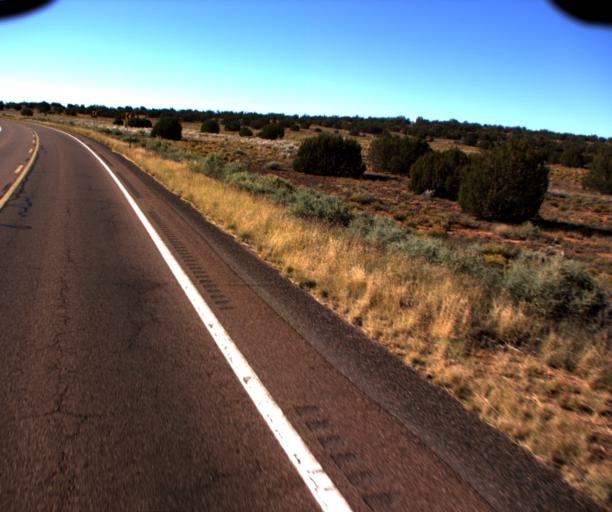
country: US
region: Arizona
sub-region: Navajo County
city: Heber-Overgaard
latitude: 34.5608
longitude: -110.4140
